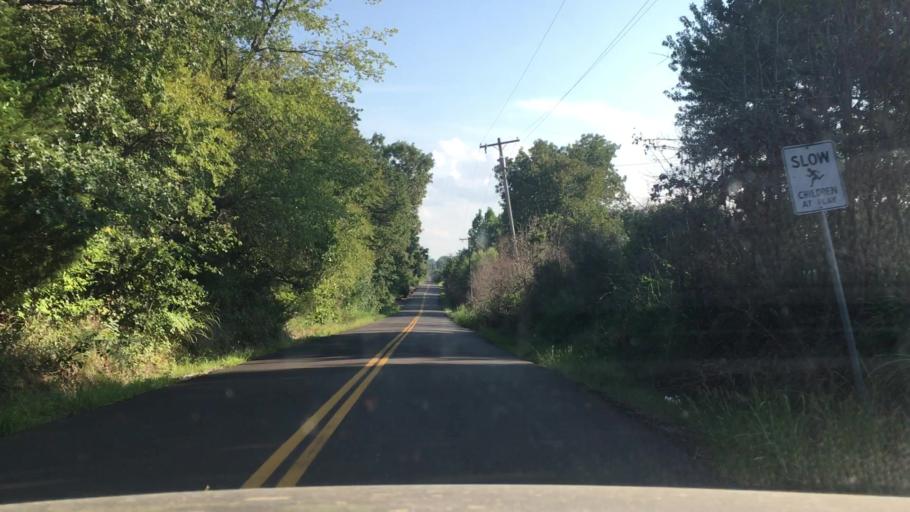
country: US
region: Oklahoma
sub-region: Muskogee County
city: Fort Gibson
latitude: 35.6527
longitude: -95.2161
